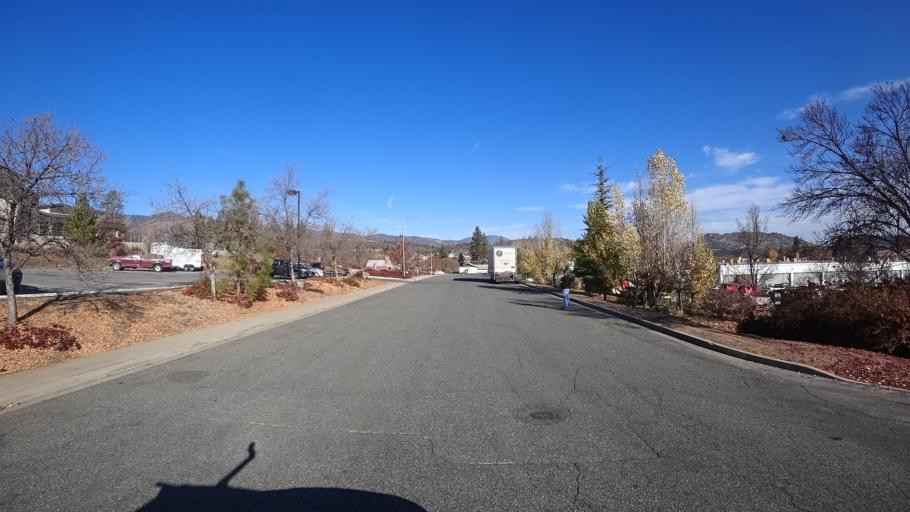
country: US
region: California
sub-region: Siskiyou County
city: Yreka
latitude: 41.7070
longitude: -122.6478
